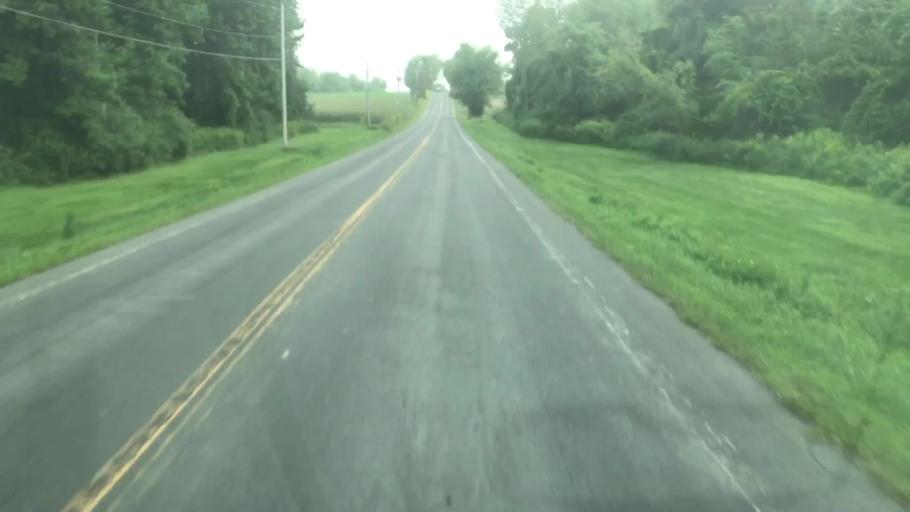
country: US
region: New York
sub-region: Onondaga County
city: Skaneateles
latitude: 42.8698
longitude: -76.4479
